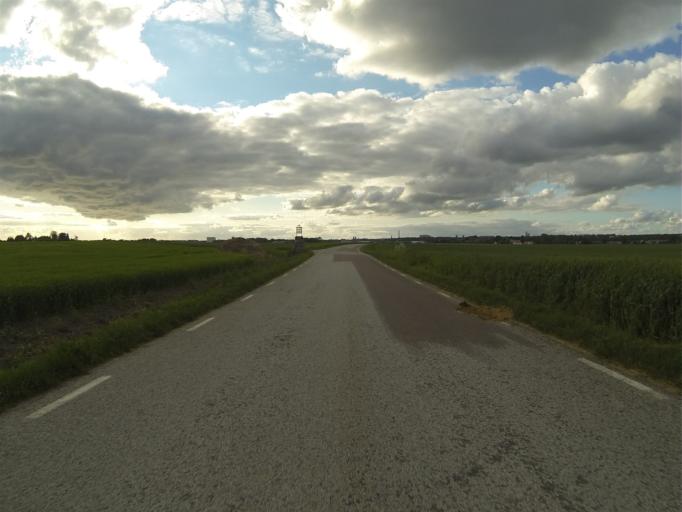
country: SE
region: Skane
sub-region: Staffanstorps Kommun
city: Staffanstorp
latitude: 55.6766
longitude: 13.2293
